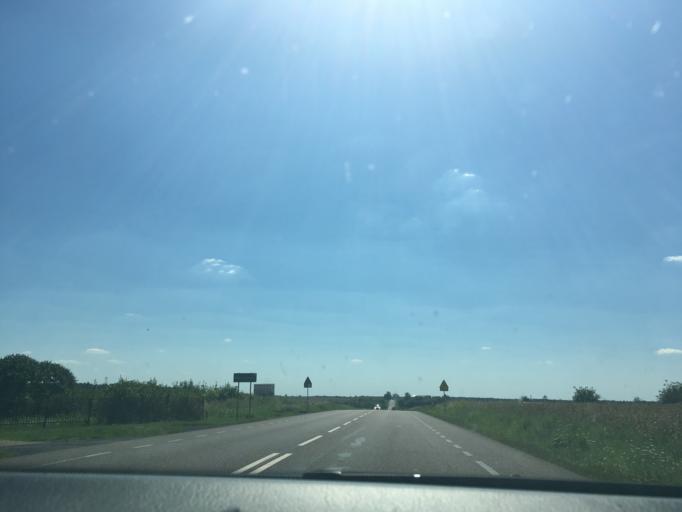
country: PL
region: Lublin Voivodeship
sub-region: Powiat janowski
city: Modliborzyce
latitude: 50.7382
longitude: 22.3503
